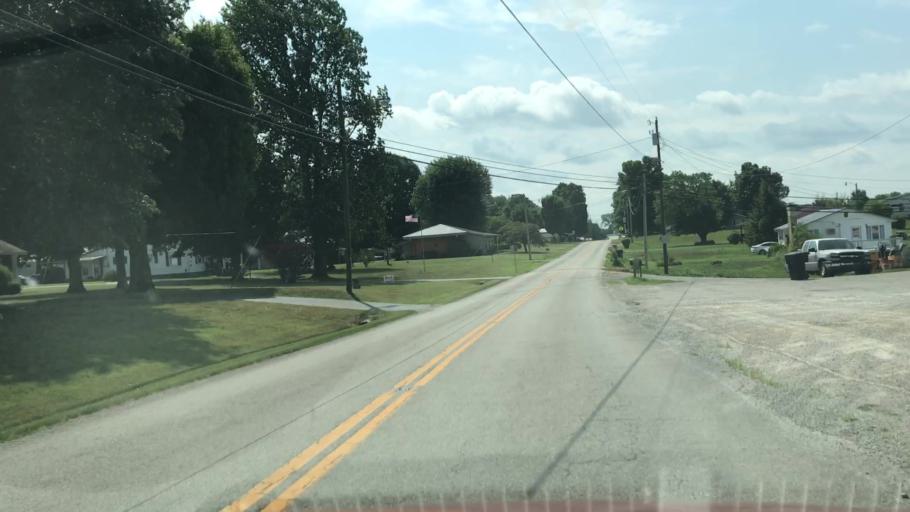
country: US
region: Kentucky
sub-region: Barren County
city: Glasgow
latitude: 36.8888
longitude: -85.8503
